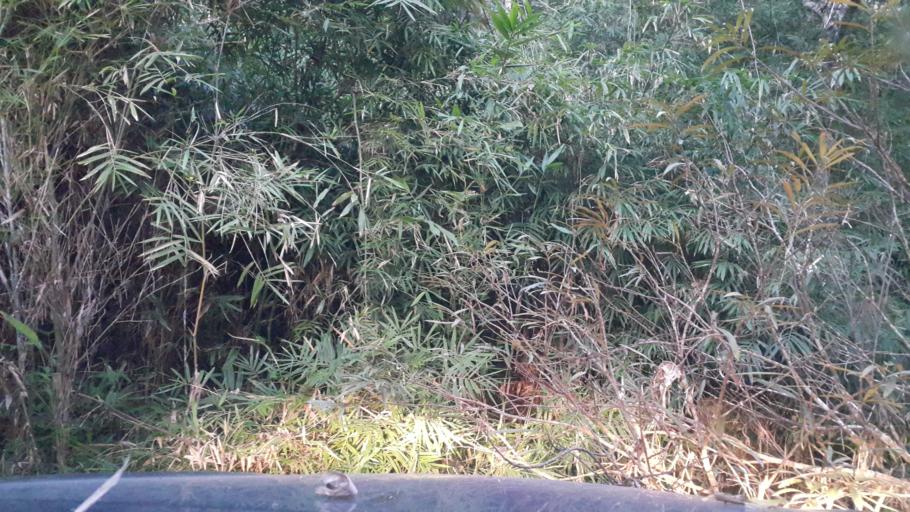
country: TH
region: Lamphun
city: Ban Thi
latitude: 18.6786
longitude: 99.2101
